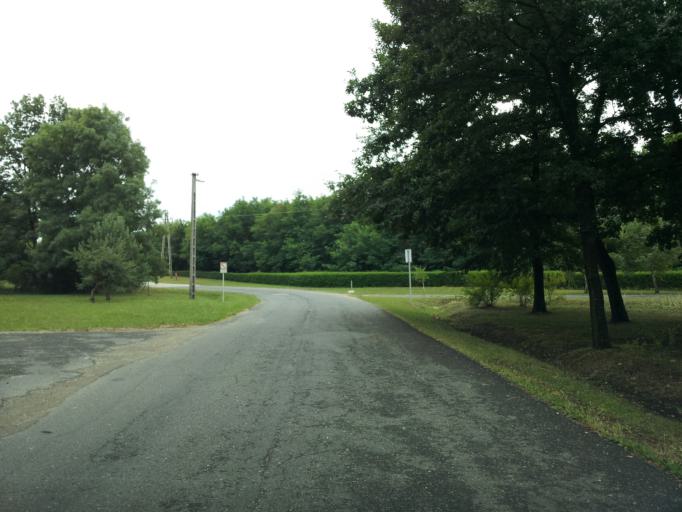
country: HU
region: Vas
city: Vasvar
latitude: 46.9840
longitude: 16.7371
